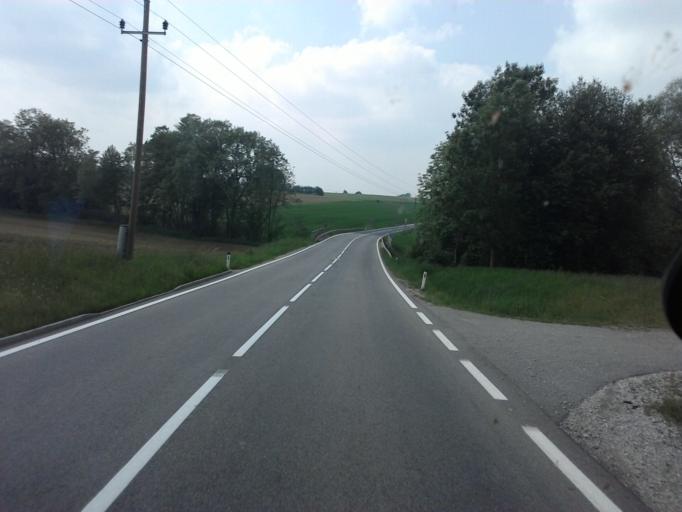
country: AT
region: Upper Austria
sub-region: Wels-Land
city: Sattledt
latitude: 48.0686
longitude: 14.0845
